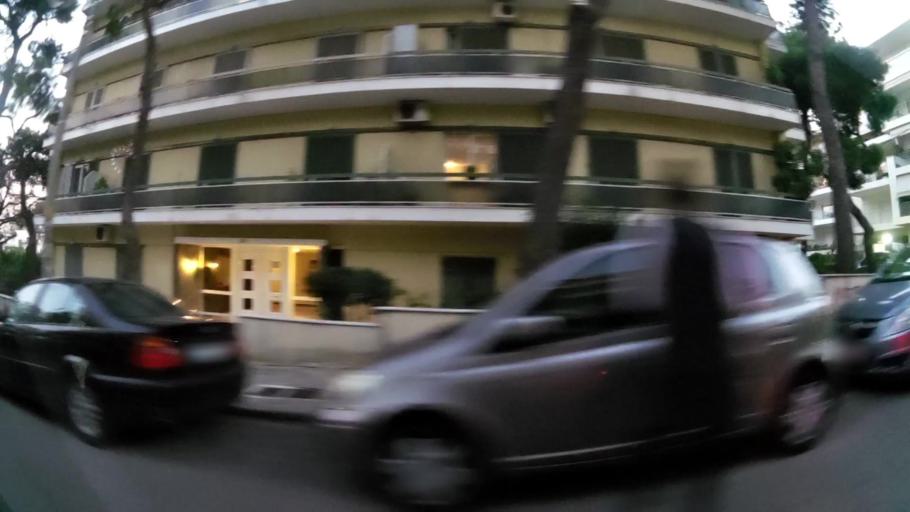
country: GR
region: Attica
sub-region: Nomarchia Athinas
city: Marousi
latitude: 38.0596
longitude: 23.8038
